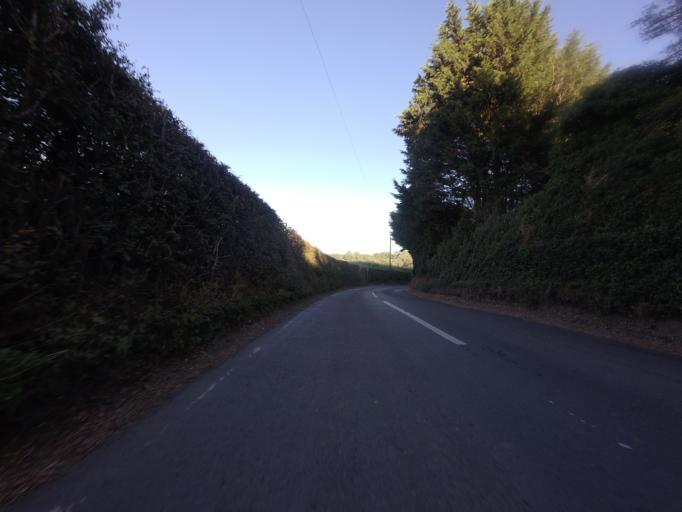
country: GB
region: England
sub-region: Kent
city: Herne Bay
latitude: 51.3317
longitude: 1.1894
